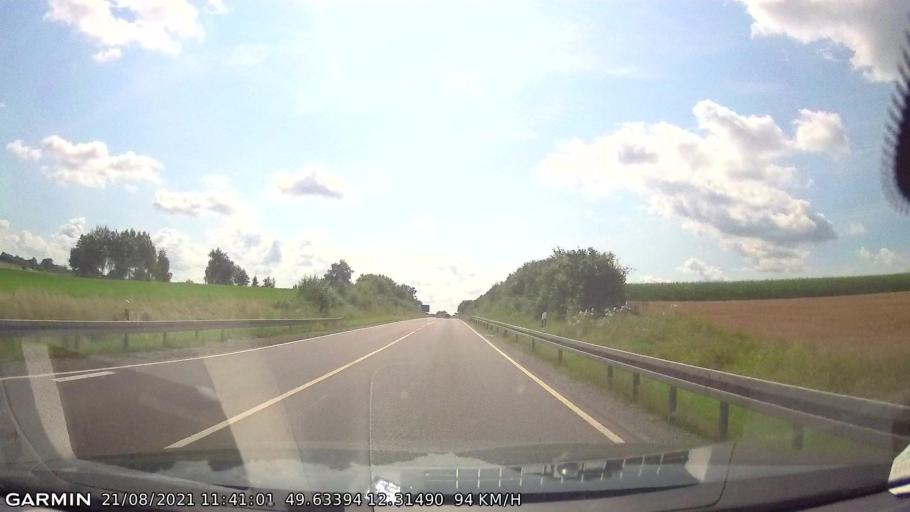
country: DE
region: Bavaria
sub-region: Upper Palatinate
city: Vohenstrauss
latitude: 49.6338
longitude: 12.3150
